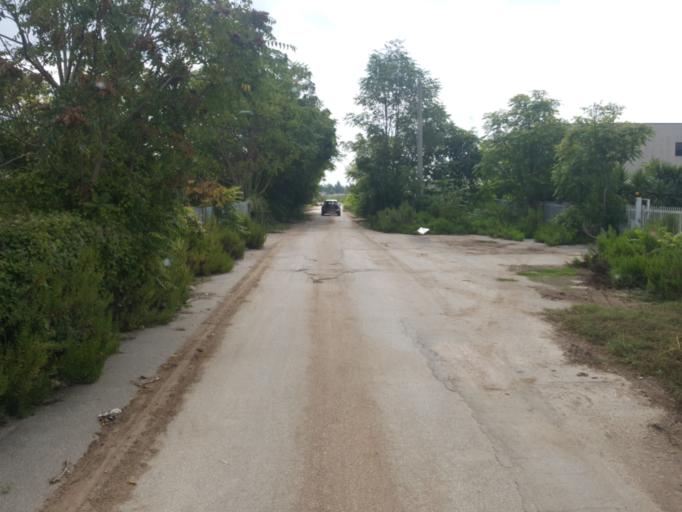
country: IT
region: Campania
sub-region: Provincia di Caserta
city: Pignataro Maggiore
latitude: 41.1744
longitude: 14.1517
